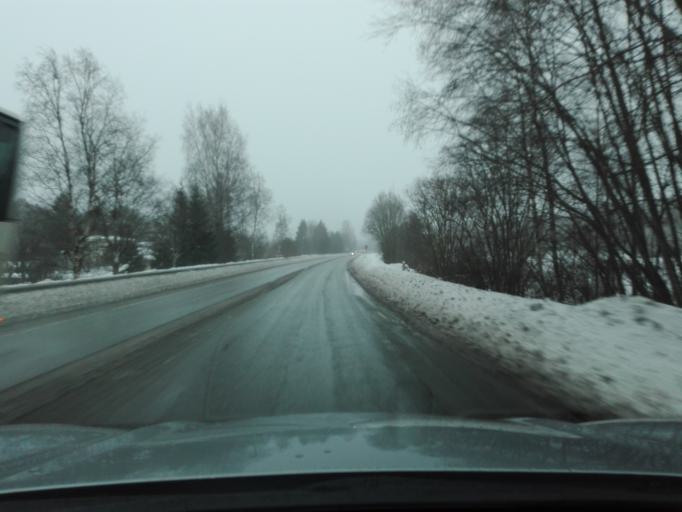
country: EE
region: Harju
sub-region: Kiili vald
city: Kiili
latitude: 59.3321
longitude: 24.7734
